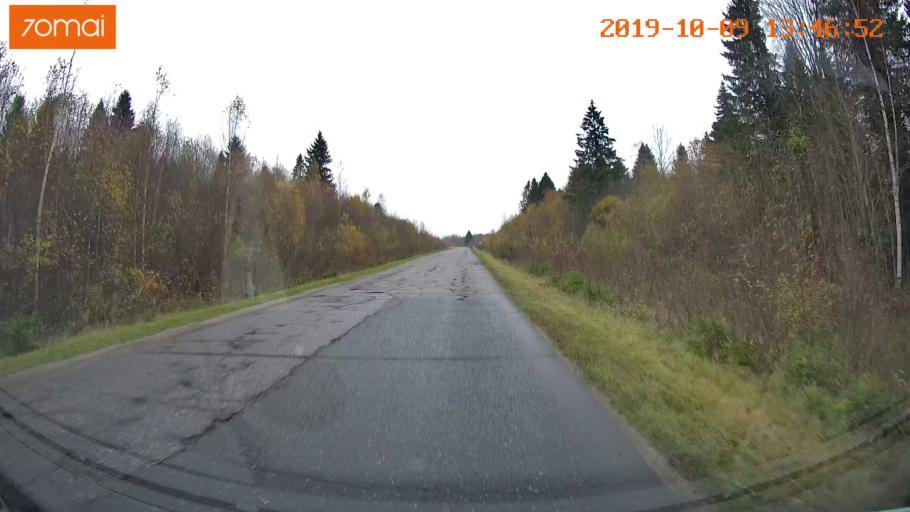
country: RU
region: Kostroma
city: Buy
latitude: 58.3869
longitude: 41.2207
